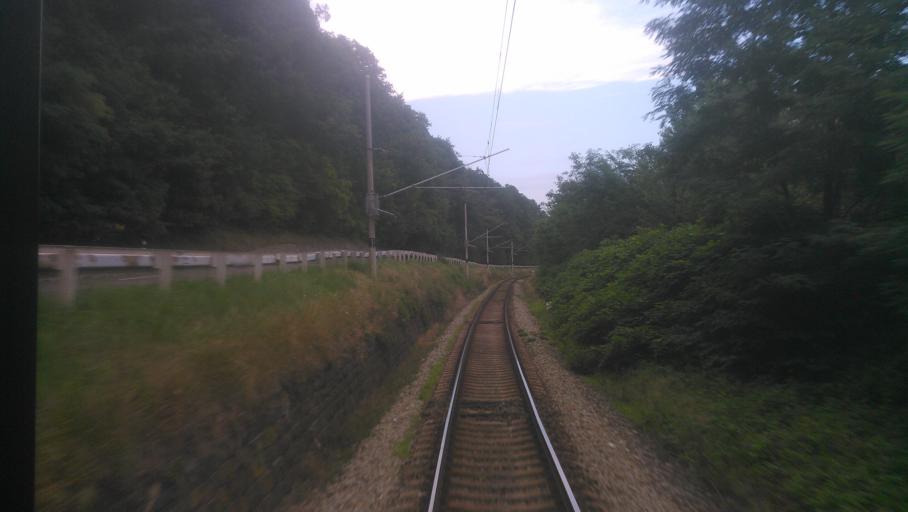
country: SK
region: Banskobystricky
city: Nova Bana
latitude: 48.3677
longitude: 18.5852
